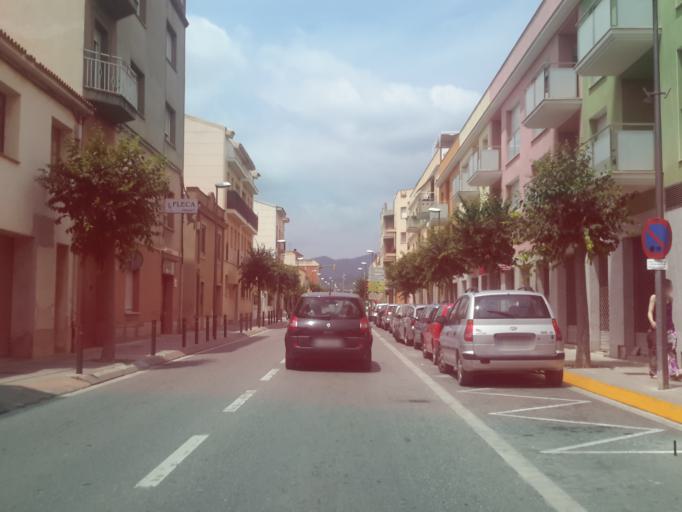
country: ES
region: Catalonia
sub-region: Provincia de Barcelona
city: Sant Marti Sarroca
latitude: 41.3863
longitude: 1.6111
